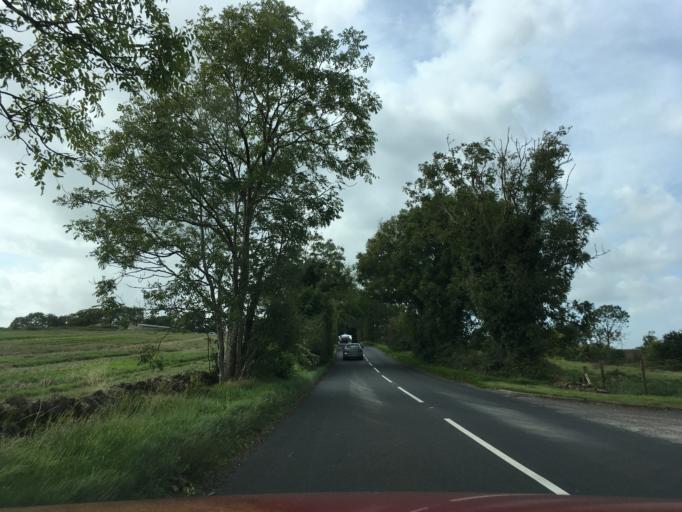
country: GB
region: England
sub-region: Gloucestershire
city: Stonehouse
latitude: 51.6990
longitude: -2.2877
